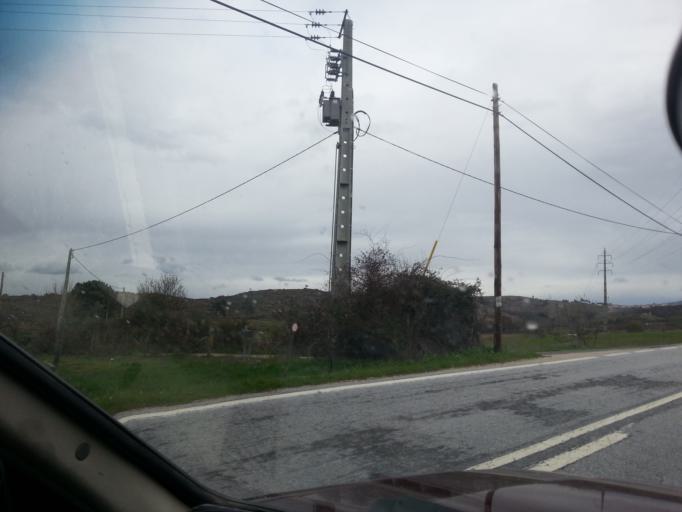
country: PT
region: Guarda
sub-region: Fornos de Algodres
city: Fornos de Algodres
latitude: 40.5534
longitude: -7.5138
